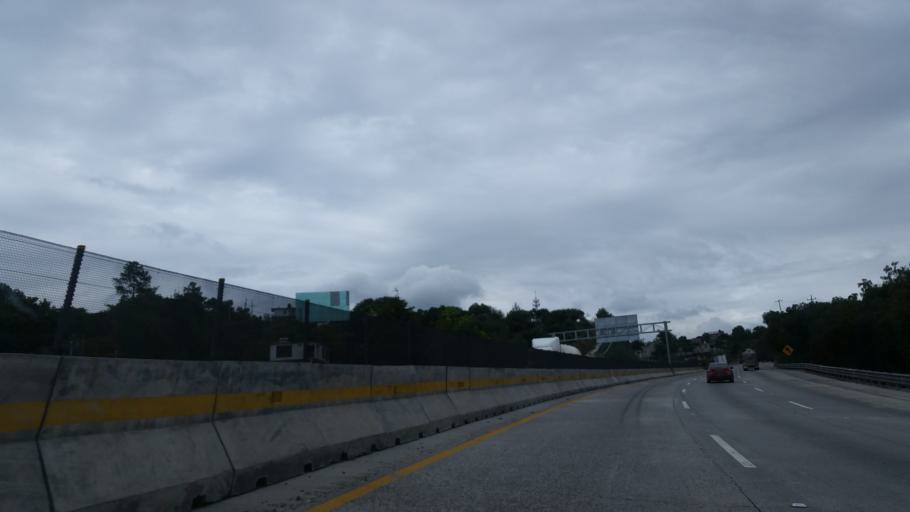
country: MX
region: Hidalgo
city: Tepeji de Ocampo
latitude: 19.9009
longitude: -99.3502
